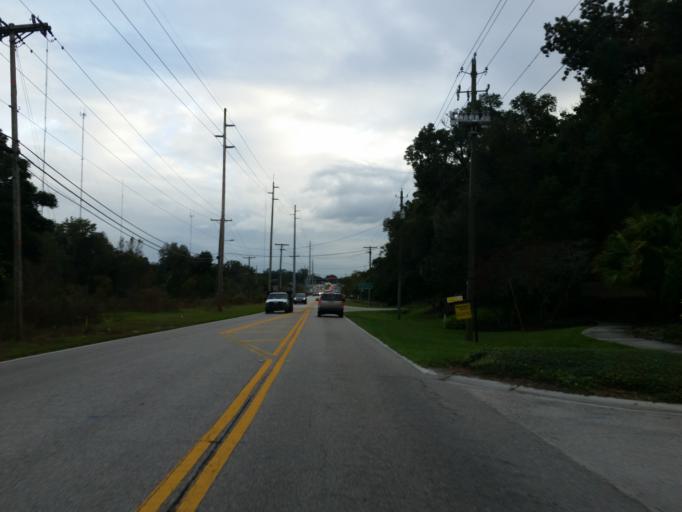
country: US
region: Florida
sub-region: Hillsborough County
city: Bloomingdale
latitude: 27.8604
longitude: -82.2693
